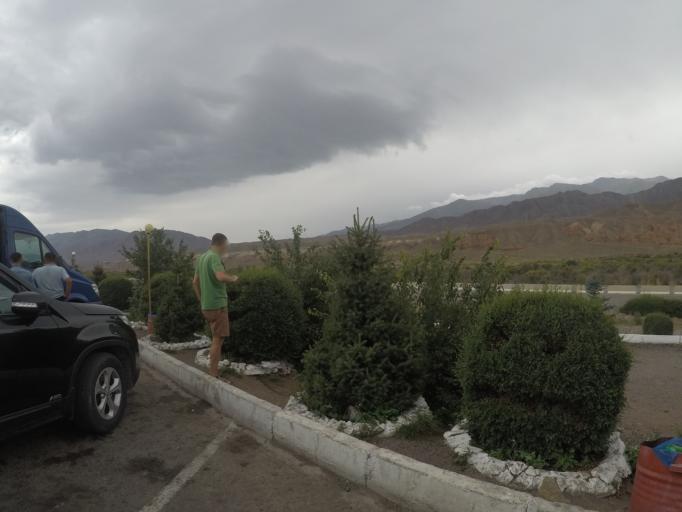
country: KG
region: Naryn
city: Kochkor
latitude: 42.5089
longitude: 75.8336
